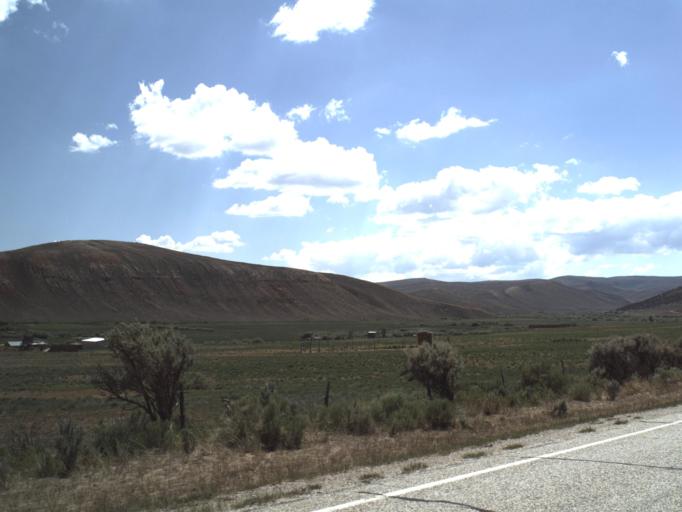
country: US
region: Utah
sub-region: Rich County
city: Randolph
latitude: 41.5047
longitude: -111.2402
